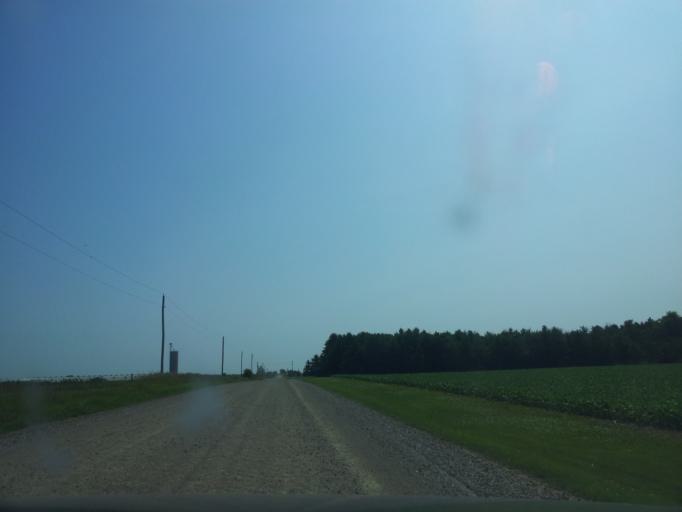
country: CA
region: Ontario
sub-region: Oxford County
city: Woodstock
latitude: 42.9490
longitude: -80.6534
